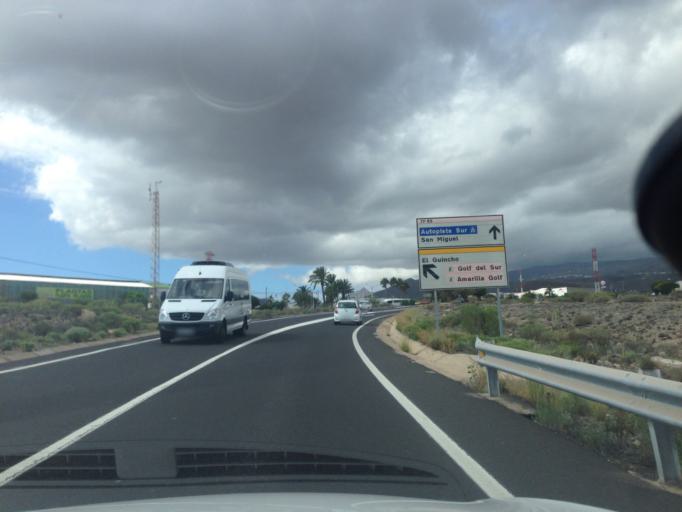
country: ES
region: Canary Islands
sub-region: Provincia de Santa Cruz de Tenerife
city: San Miguel
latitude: 28.0460
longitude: -16.6096
